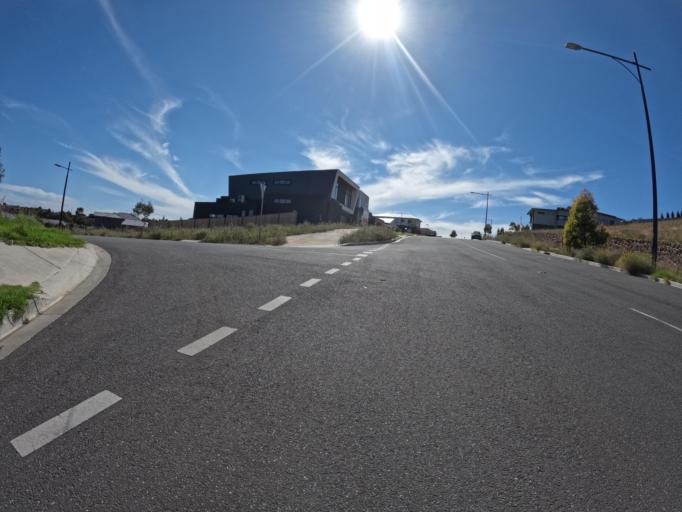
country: AU
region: Victoria
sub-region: Greater Geelong
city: Hamlyn Heights
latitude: -38.1332
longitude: 144.3142
